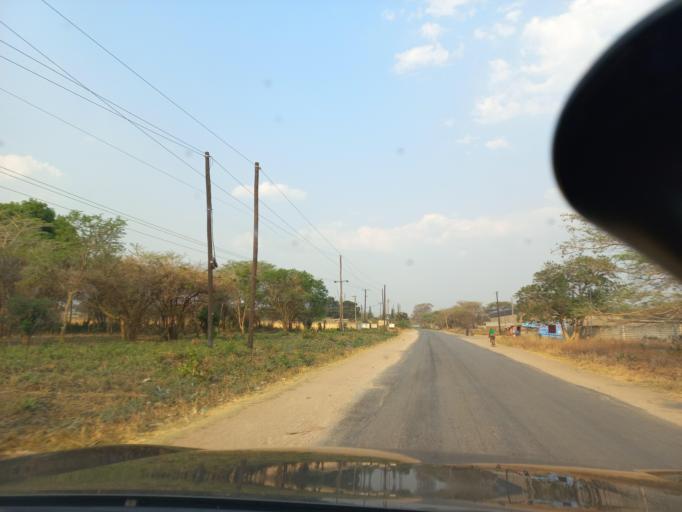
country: ZM
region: Lusaka
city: Lusaka
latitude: -15.4779
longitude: 28.2035
